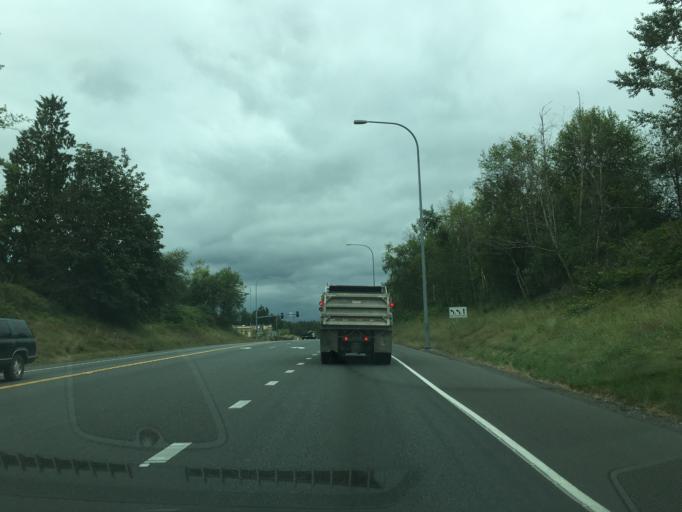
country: US
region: Washington
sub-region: Snohomish County
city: West Lake Stevens
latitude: 48.0519
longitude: -122.1108
